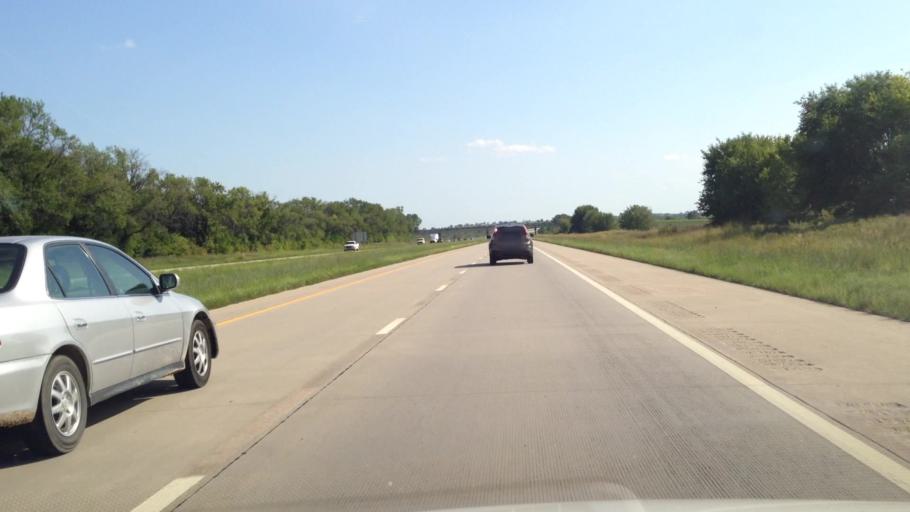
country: US
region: Kansas
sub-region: Bourbon County
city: Fort Scott
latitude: 37.9842
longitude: -94.7047
